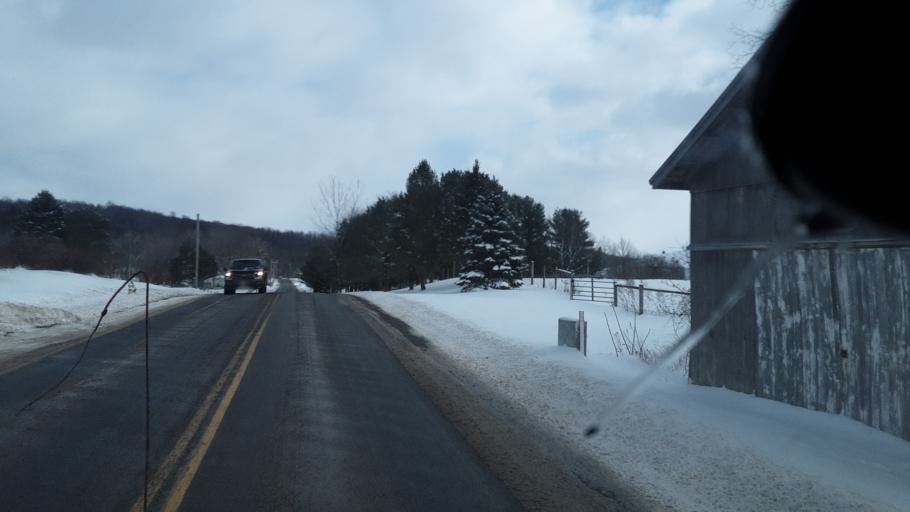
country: US
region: New York
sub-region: Wayne County
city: Lyons
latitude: 43.0902
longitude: -77.0482
